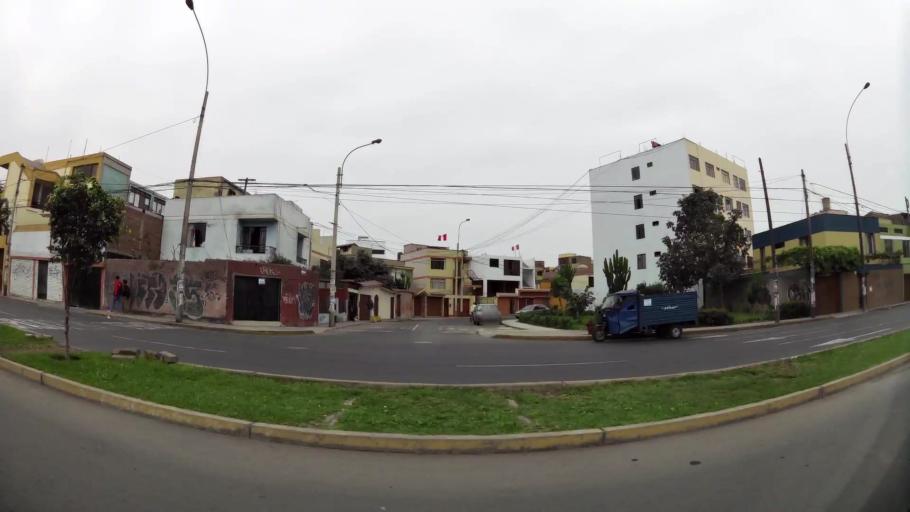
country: PE
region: Callao
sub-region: Callao
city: Callao
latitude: -12.0525
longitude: -77.0787
